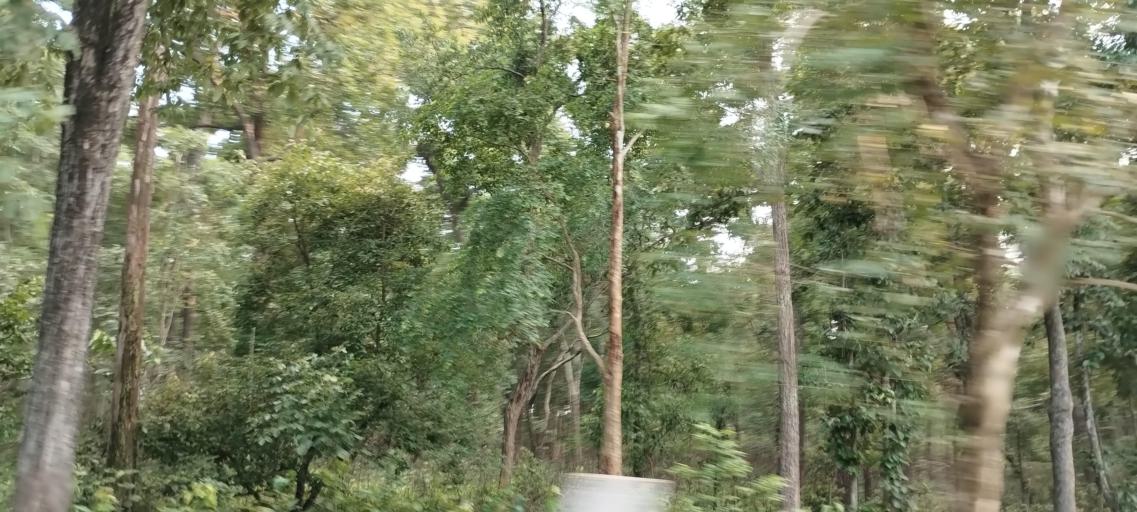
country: NP
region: Mid Western
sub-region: Bheri Zone
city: Bardiya
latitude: 28.4289
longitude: 81.3714
